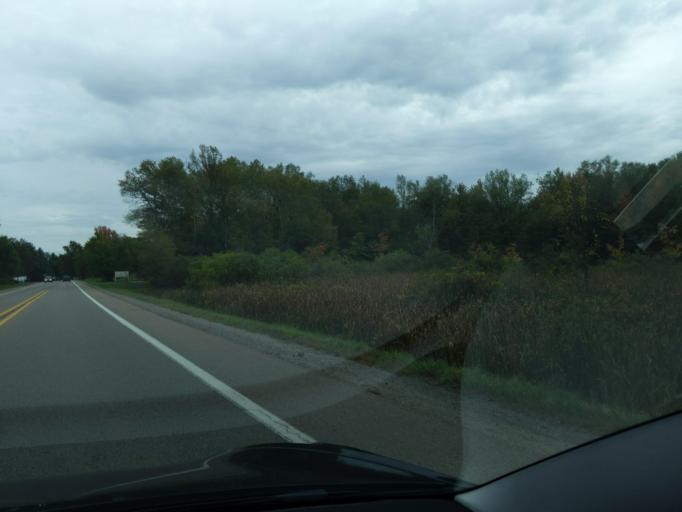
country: US
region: Michigan
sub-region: Clare County
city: Clare
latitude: 43.8415
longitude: -84.8849
